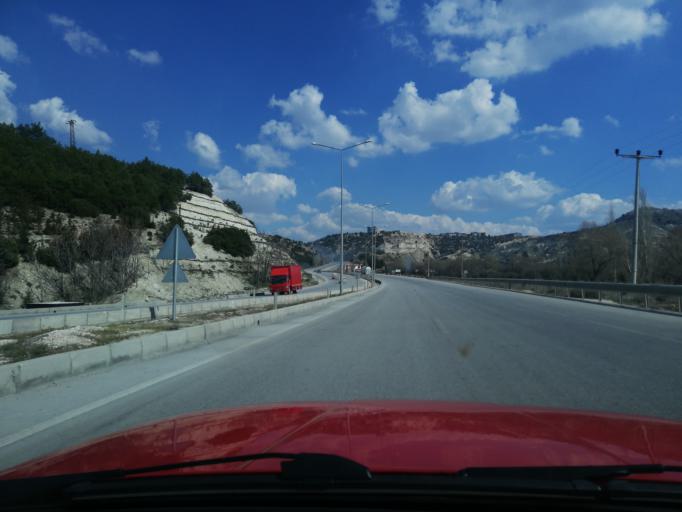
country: TR
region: Burdur
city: Burdur
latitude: 37.6993
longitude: 30.3212
